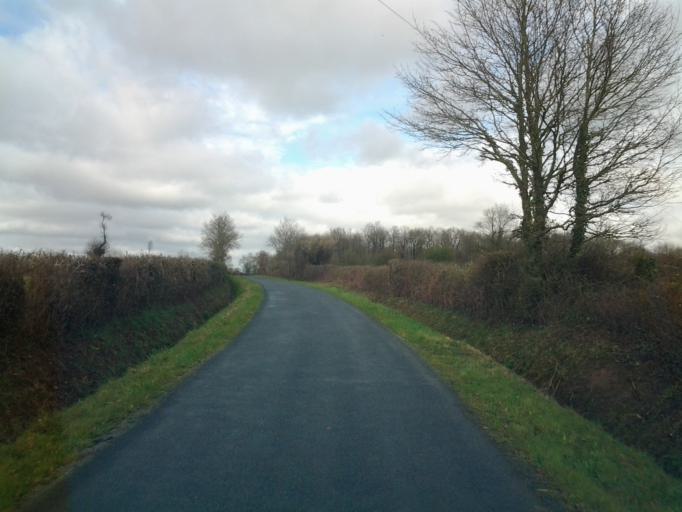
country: FR
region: Pays de la Loire
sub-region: Departement de la Vendee
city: Nesmy
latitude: 46.6482
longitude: -1.3631
